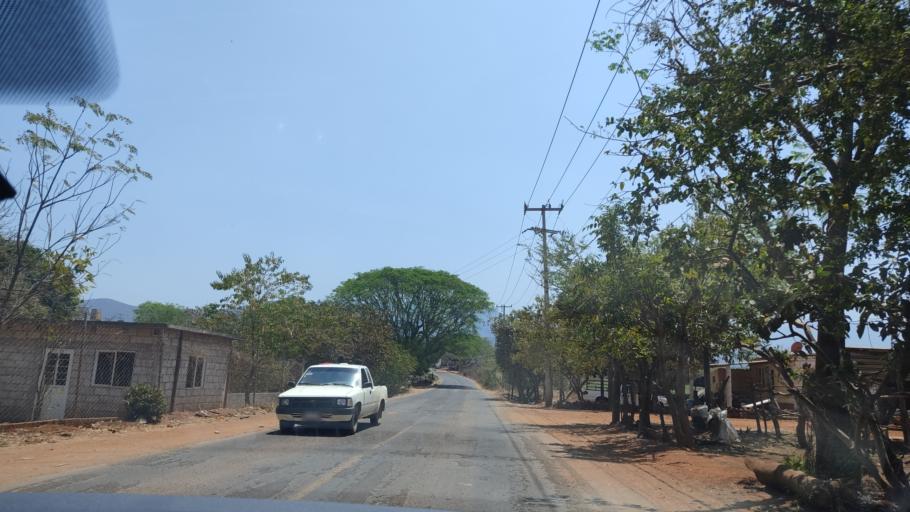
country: MX
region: Nayarit
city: Puga
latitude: 21.5780
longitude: -104.7873
